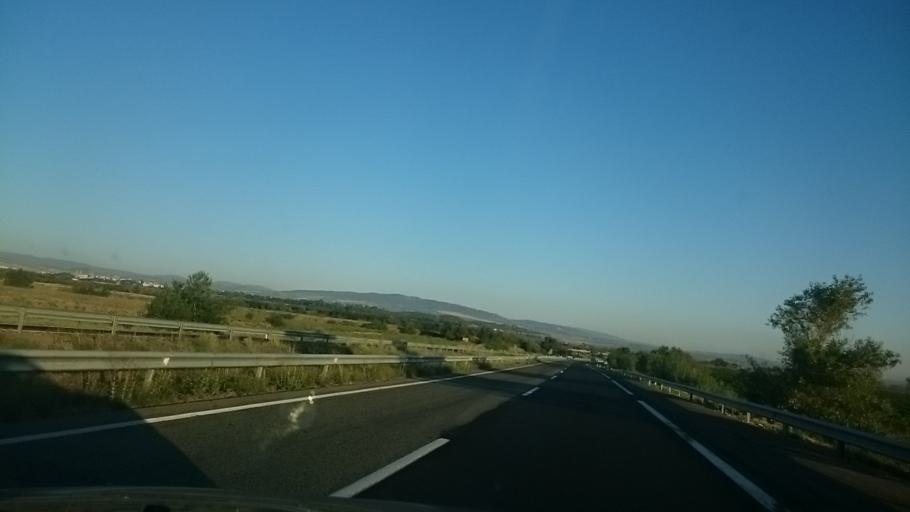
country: ES
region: Navarre
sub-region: Provincia de Navarra
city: Corella
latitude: 42.1227
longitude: -1.7467
